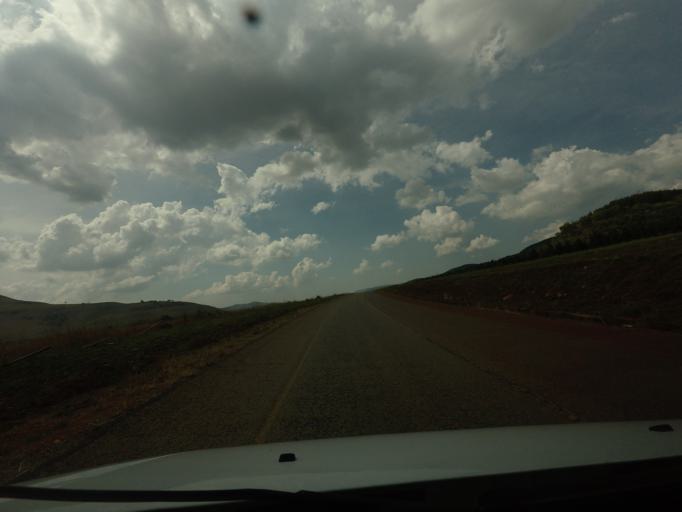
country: ZA
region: Mpumalanga
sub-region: Ehlanzeni District
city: Graksop
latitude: -24.7084
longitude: 30.8180
